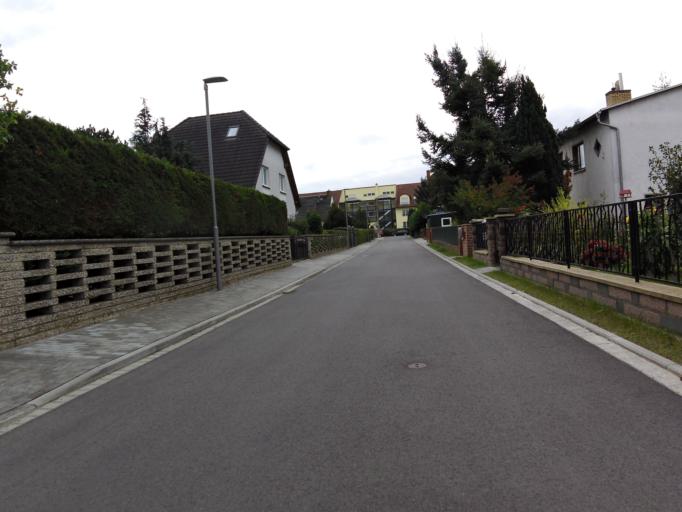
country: DE
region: Saxony
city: Grossposna
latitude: 51.3138
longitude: 12.4647
